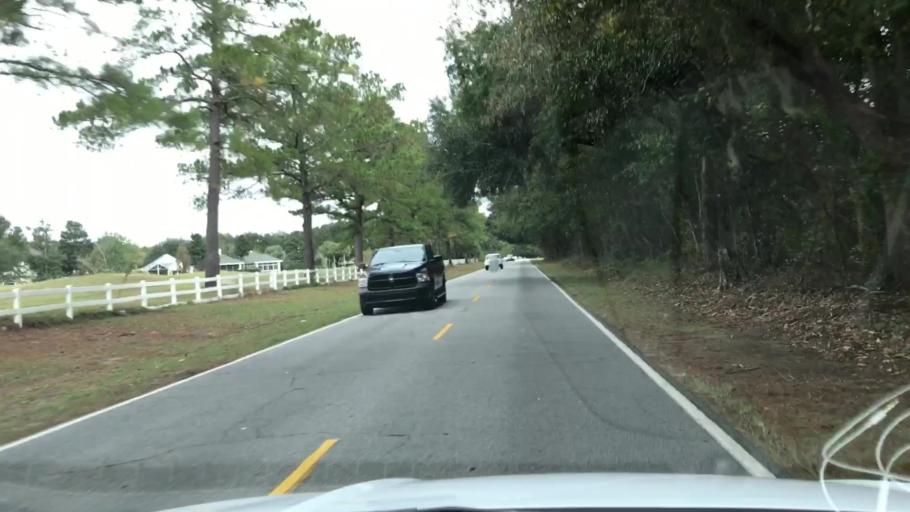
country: US
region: South Carolina
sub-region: Beaufort County
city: Bluffton
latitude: 32.2682
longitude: -80.8798
